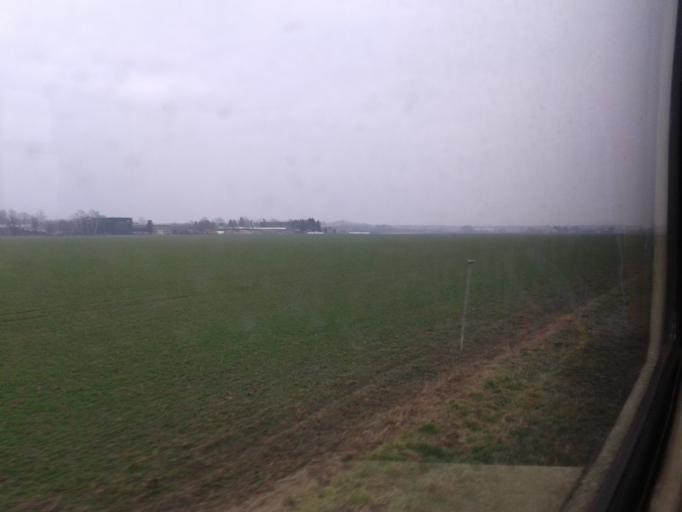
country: CZ
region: Olomoucky
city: Prikazy
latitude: 49.6380
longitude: 17.1525
